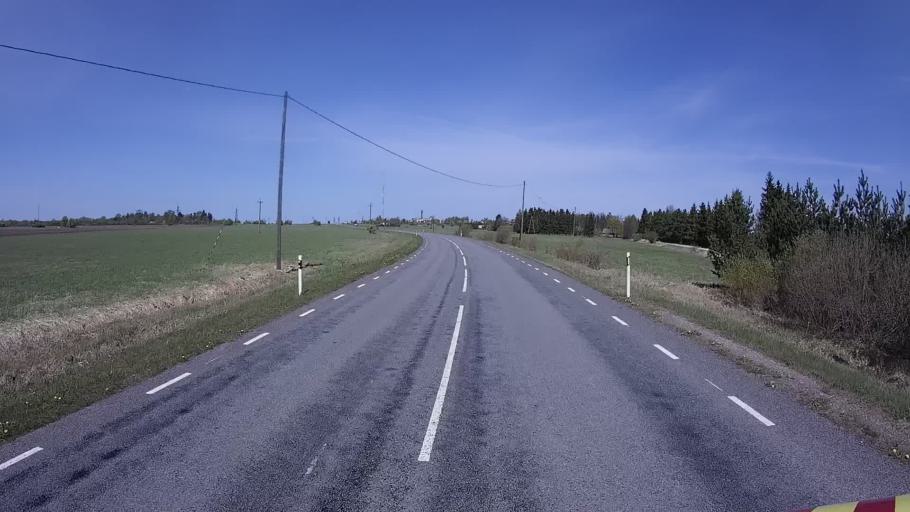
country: EE
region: Laeaene
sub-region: Lihula vald
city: Lihula
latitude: 58.6667
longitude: 23.8335
